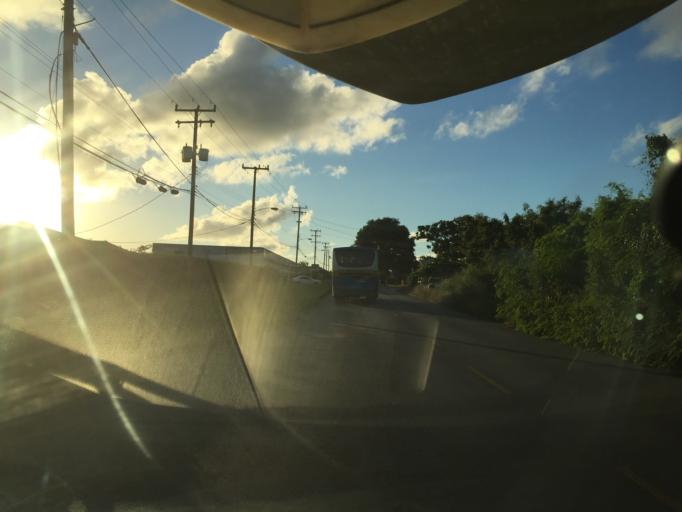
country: BB
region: Christ Church
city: Oistins
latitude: 13.0804
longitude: -59.4940
